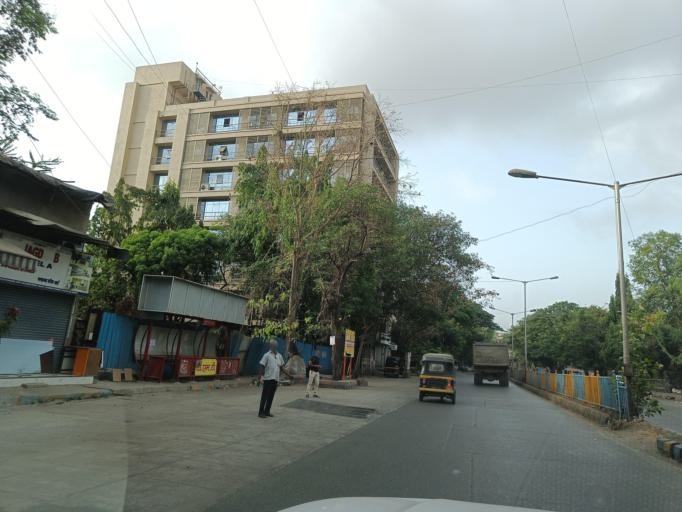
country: IN
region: Maharashtra
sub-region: Thane
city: Thane
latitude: 19.2106
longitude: 72.9773
